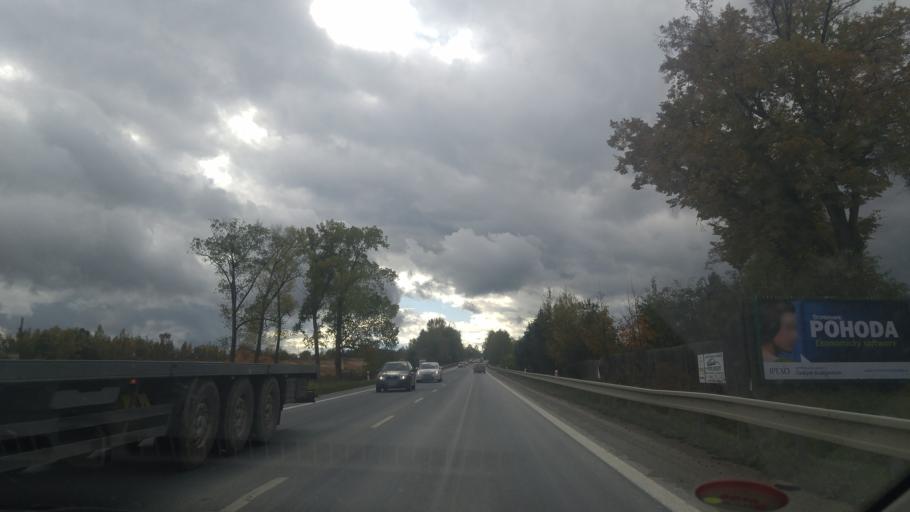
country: CZ
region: Jihocesky
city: Sevetin
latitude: 49.1302
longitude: 14.6081
